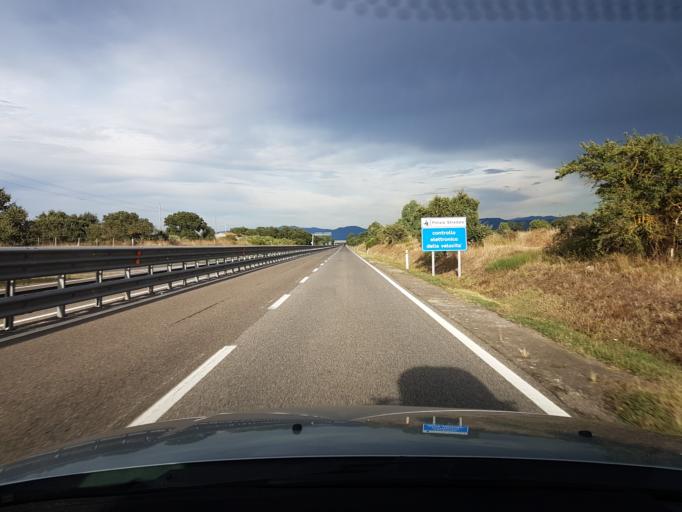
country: IT
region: Sardinia
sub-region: Provincia di Oristano
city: Abbasanta
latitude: 40.1148
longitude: 8.8208
